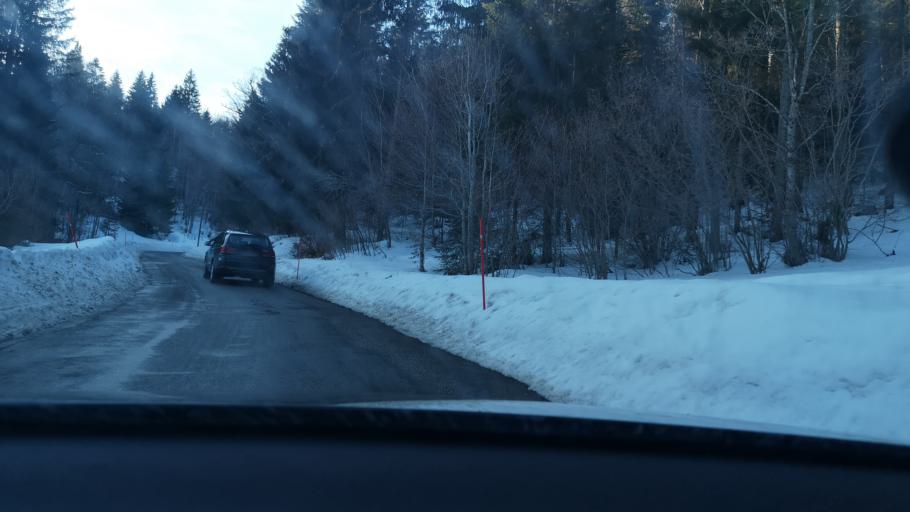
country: FR
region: Franche-Comte
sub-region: Departement du Doubs
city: Montlebon
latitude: 46.9780
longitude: 6.5639
